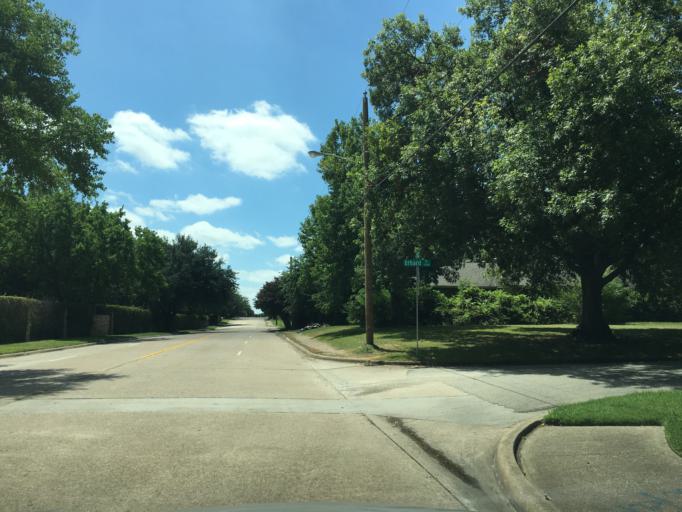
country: US
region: Texas
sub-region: Dallas County
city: Garland
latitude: 32.8414
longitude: -96.6527
